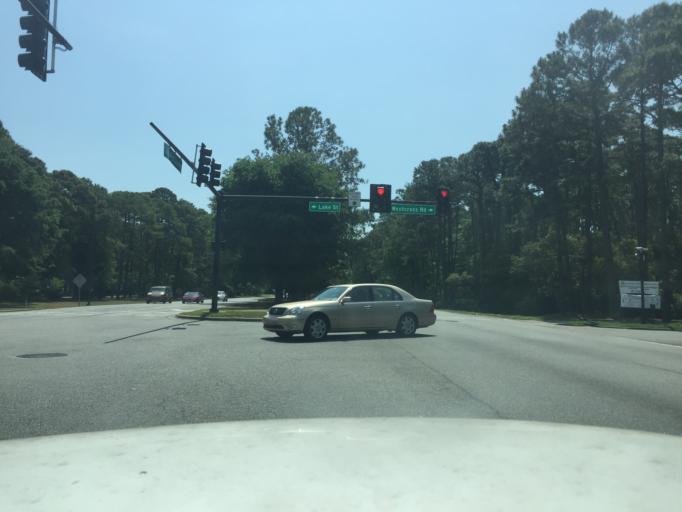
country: US
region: Georgia
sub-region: Chatham County
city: Skidaway Island
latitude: 31.9387
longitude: -81.0545
